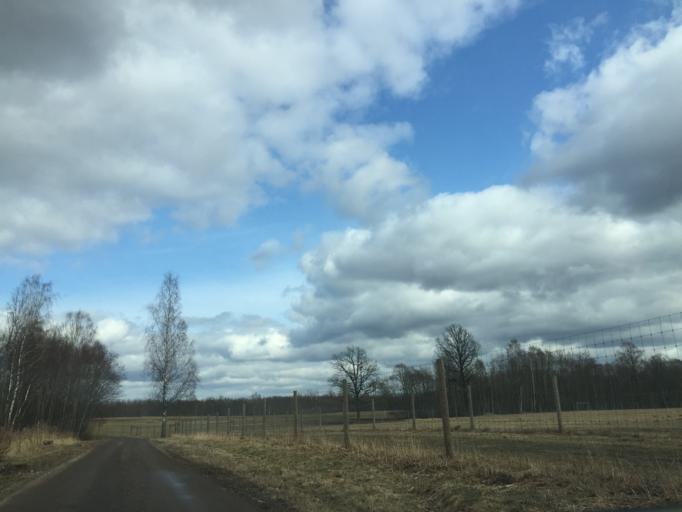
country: LV
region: Vecumnieki
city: Vecumnieki
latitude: 56.5326
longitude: 24.6887
